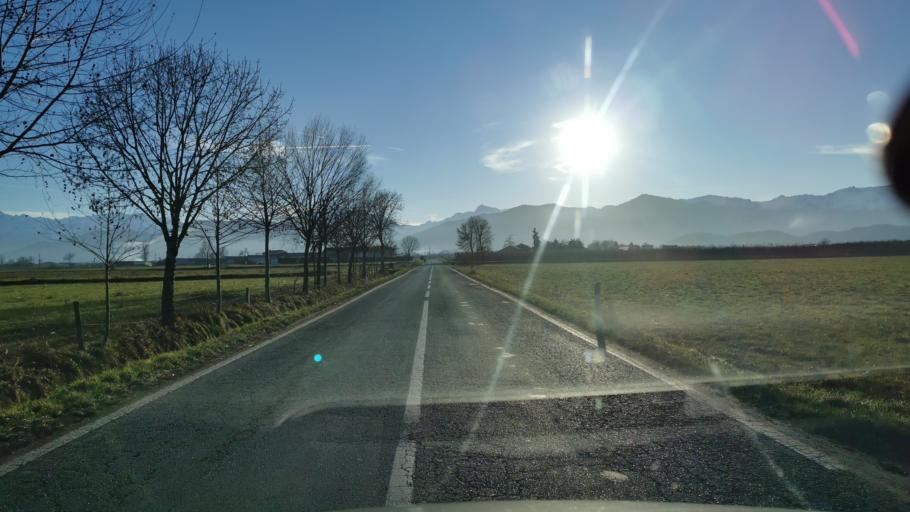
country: IT
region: Piedmont
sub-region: Provincia di Cuneo
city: Caraglio
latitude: 44.4436
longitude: 7.4692
